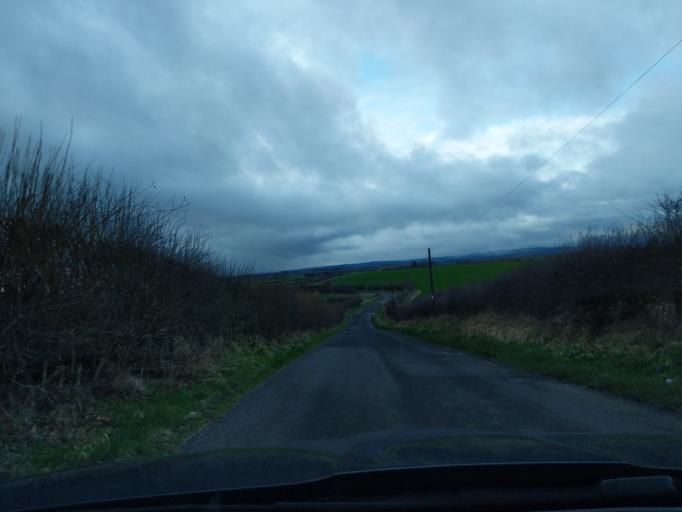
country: GB
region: England
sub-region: Northumberland
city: Ford
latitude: 55.7122
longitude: -2.1085
